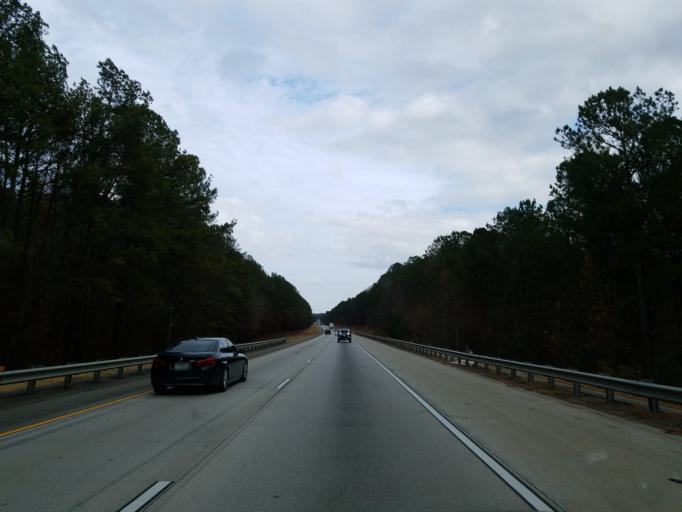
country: US
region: Georgia
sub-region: Carroll County
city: Mount Zion
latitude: 33.6873
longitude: -85.2271
